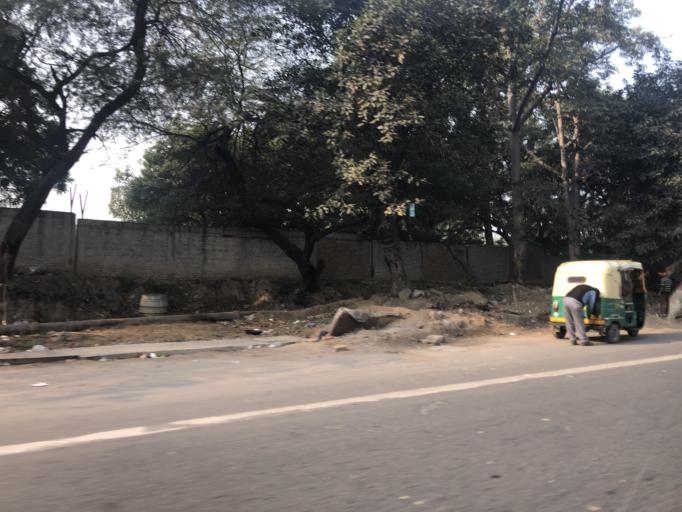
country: IN
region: NCT
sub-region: Central Delhi
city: Karol Bagh
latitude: 28.6006
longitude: 77.1607
